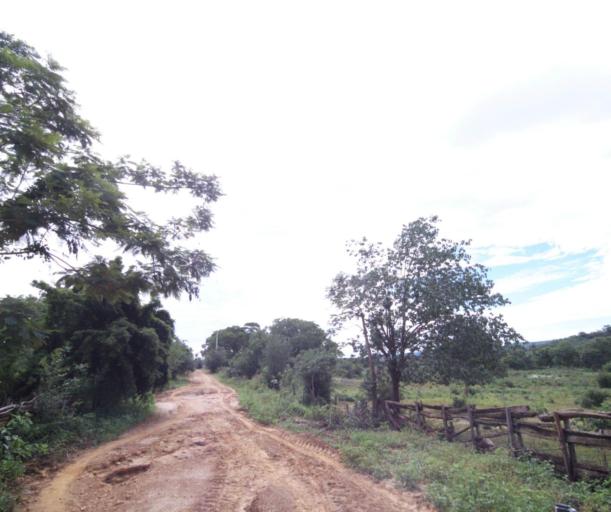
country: BR
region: Bahia
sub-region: Carinhanha
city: Carinhanha
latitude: -14.2399
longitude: -44.3962
